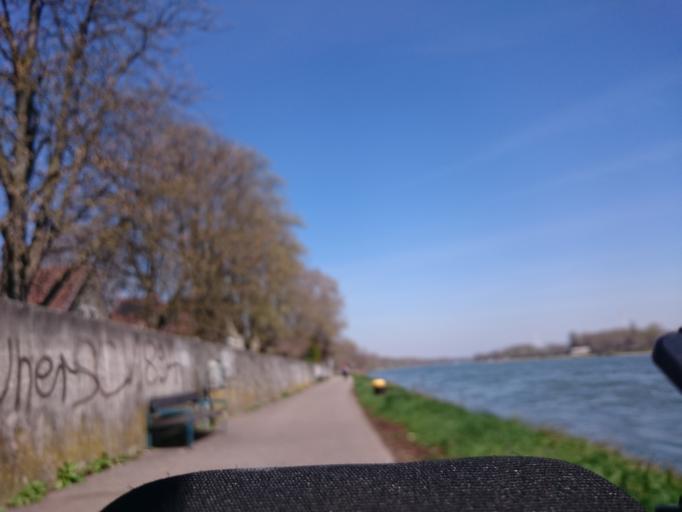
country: DE
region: Rheinland-Pfalz
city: Worth am Rhein
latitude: 49.0374
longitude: 8.3016
